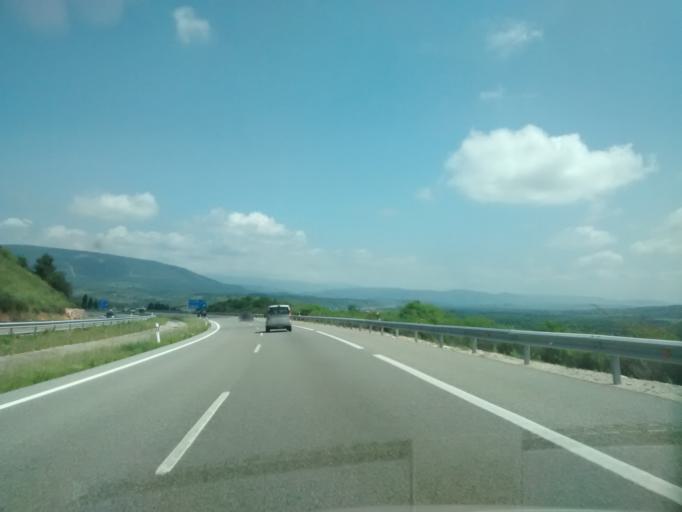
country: ES
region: Castille and Leon
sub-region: Provincia de Leon
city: Molinaseca
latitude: 42.5770
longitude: -6.5314
